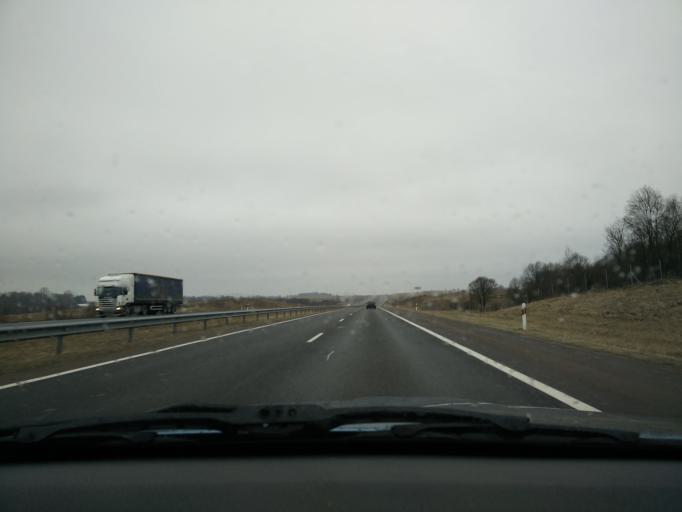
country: LT
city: Silale
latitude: 55.5813
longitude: 22.1532
